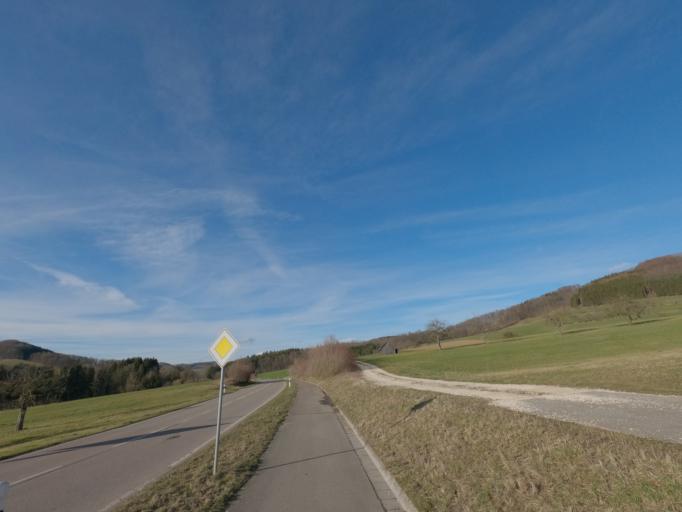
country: DE
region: Baden-Wuerttemberg
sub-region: Regierungsbezirk Stuttgart
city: Donzdorf
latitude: 48.6957
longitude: 9.8023
